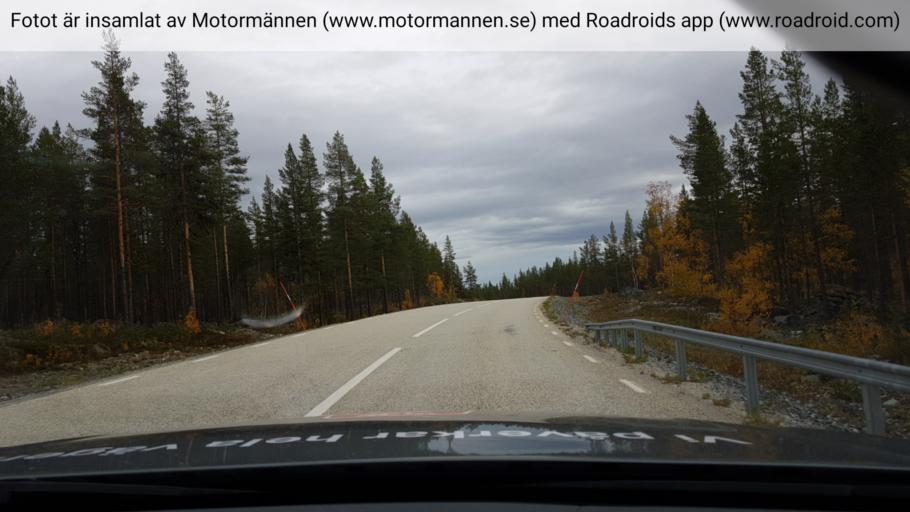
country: SE
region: Jaemtland
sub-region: Are Kommun
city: Jarpen
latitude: 62.8452
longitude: 13.4005
